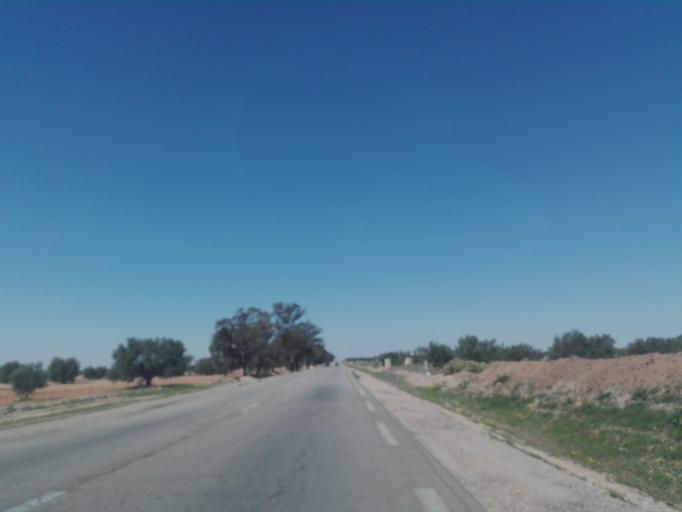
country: TN
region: Safaqis
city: Bi'r `Ali Bin Khalifah
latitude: 34.7576
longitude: 10.3167
